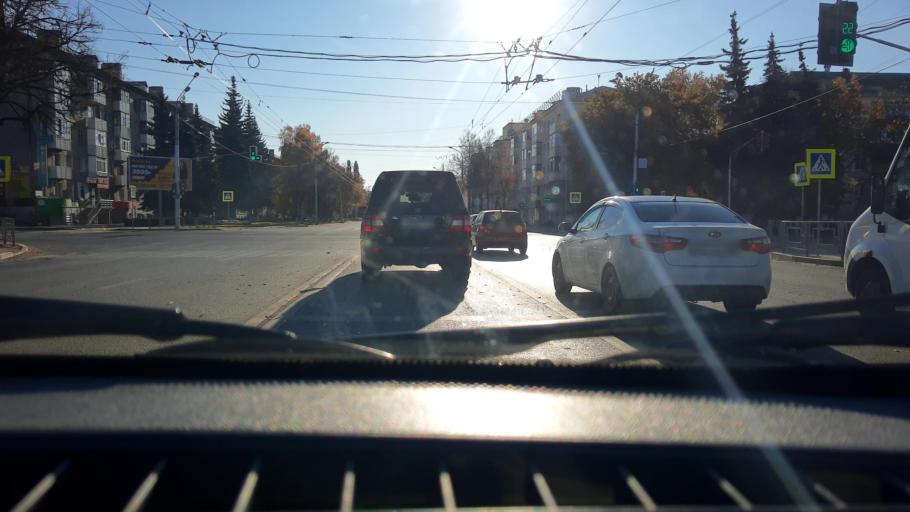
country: RU
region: Bashkortostan
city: Ufa
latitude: 54.8135
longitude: 56.0889
